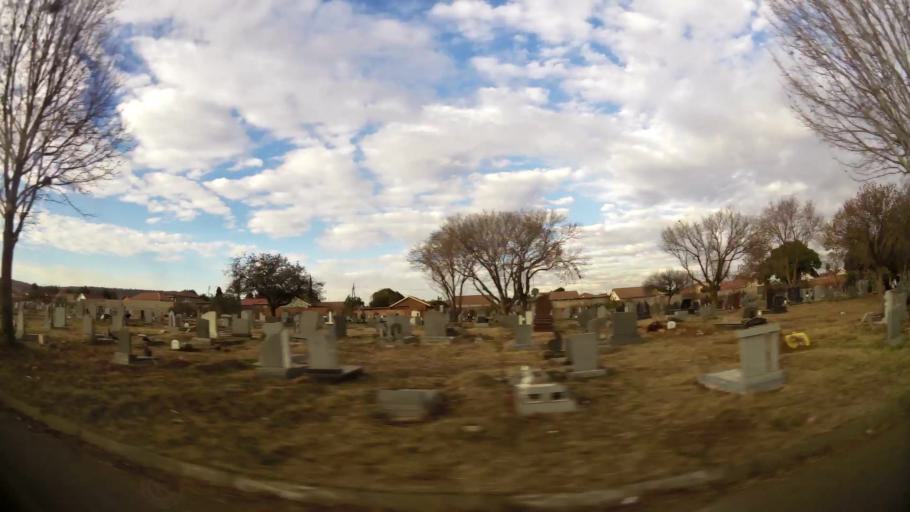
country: ZA
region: Gauteng
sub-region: City of Tshwane Metropolitan Municipality
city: Pretoria
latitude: -25.7105
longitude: 28.3252
